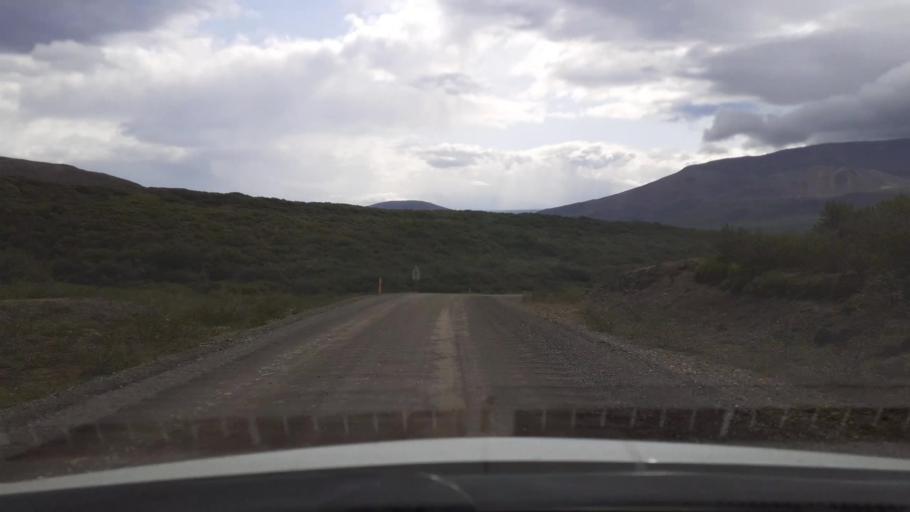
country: IS
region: West
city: Borgarnes
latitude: 64.5583
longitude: -21.6256
